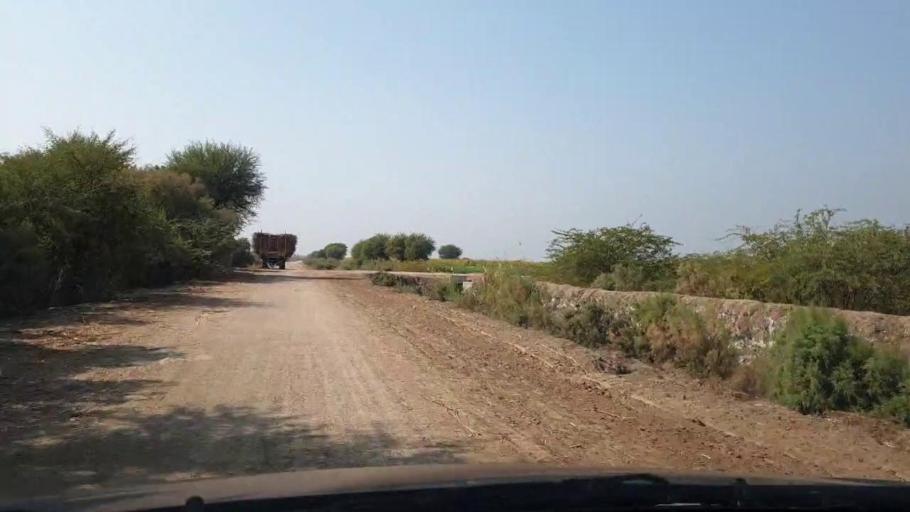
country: PK
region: Sindh
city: Jhol
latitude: 25.8922
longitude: 68.9483
